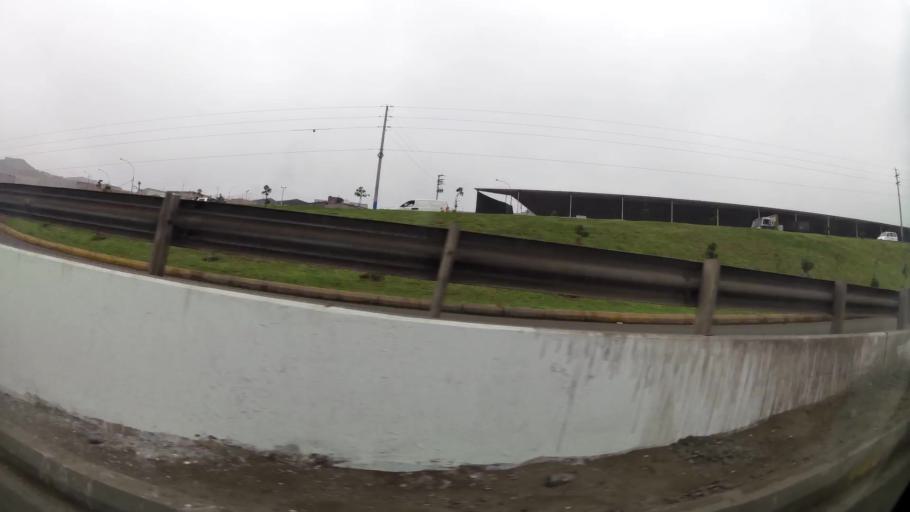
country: PE
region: Lima
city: Ventanilla
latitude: -11.8527
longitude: -77.1293
